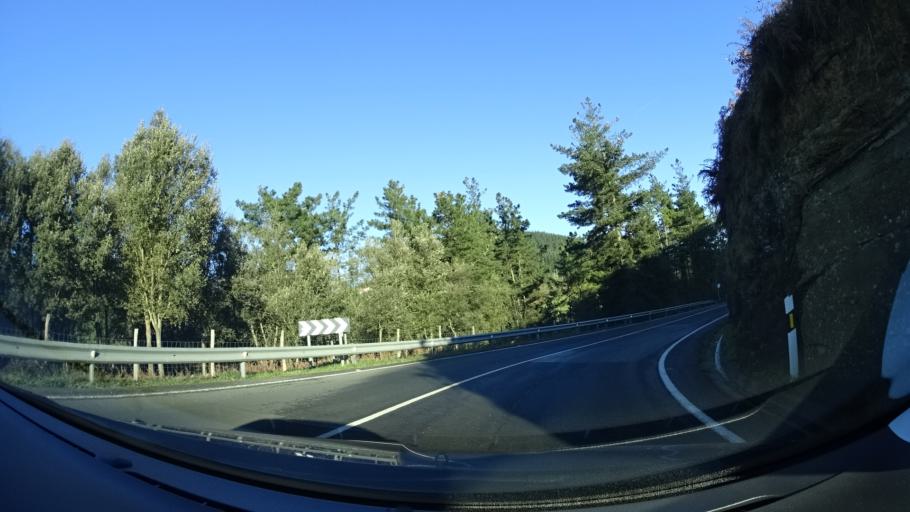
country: ES
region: Basque Country
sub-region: Bizkaia
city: Berriatua
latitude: 43.3153
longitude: -2.4818
